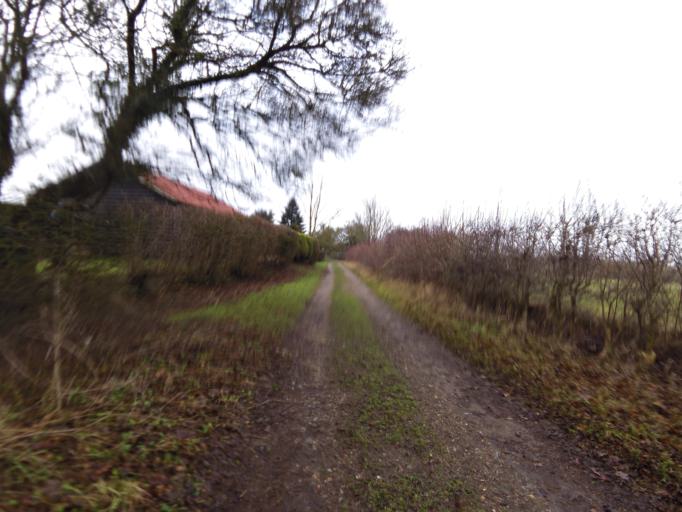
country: GB
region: England
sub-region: Suffolk
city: Needham Market
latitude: 52.1591
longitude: 1.0656
